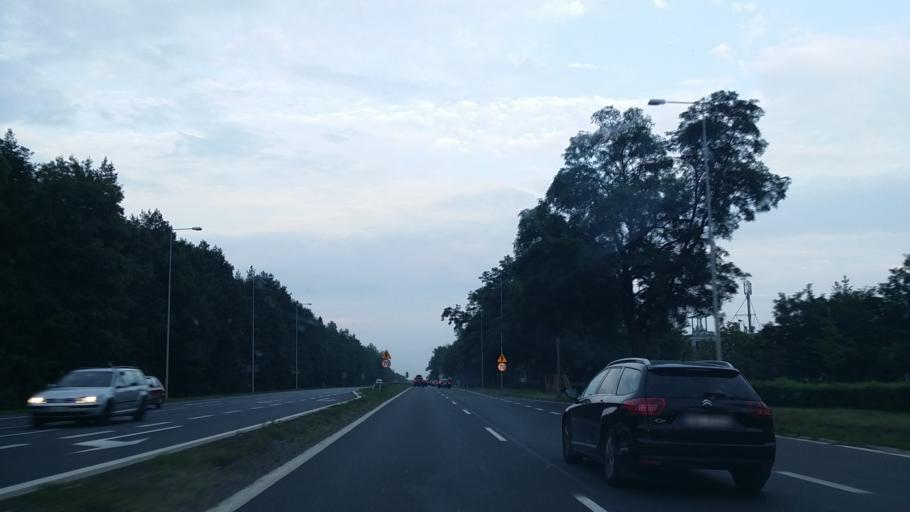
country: PL
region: Lower Silesian Voivodeship
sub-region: Powiat lubinski
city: Lubin
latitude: 51.4373
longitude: 16.1546
